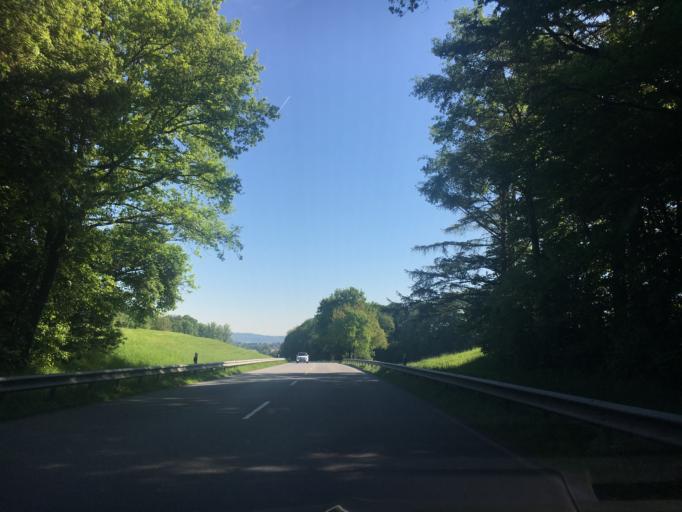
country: DE
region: Bavaria
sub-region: Upper Bavaria
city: Altoetting
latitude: 48.2047
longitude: 12.6507
